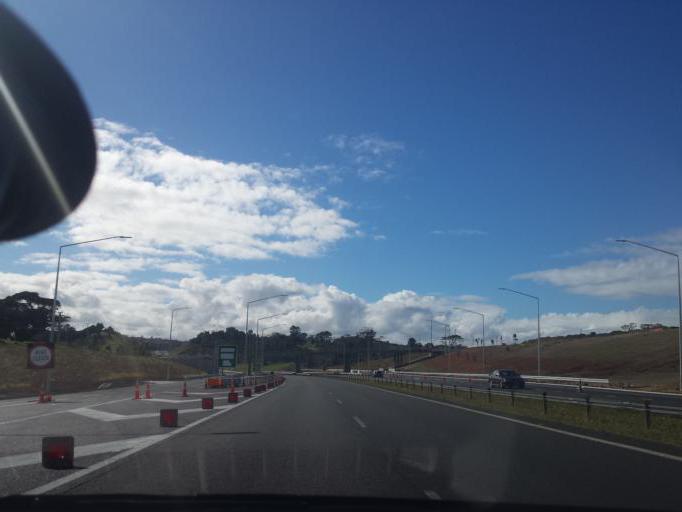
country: NZ
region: Auckland
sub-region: Auckland
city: Rothesay Bay
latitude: -36.6056
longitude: 174.6613
